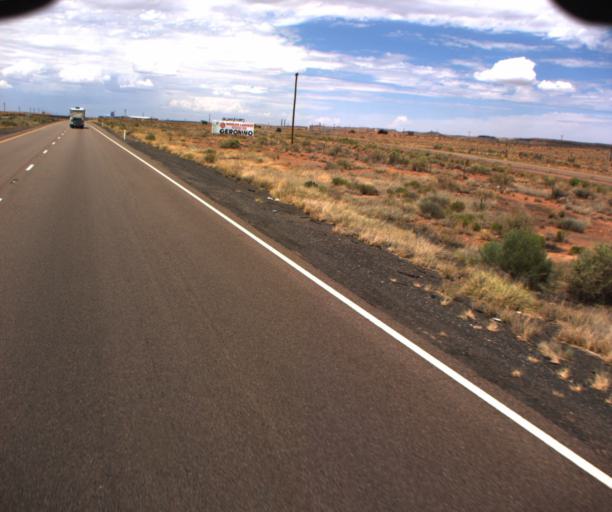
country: US
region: Arizona
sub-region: Navajo County
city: Holbrook
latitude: 34.9084
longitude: -110.2199
